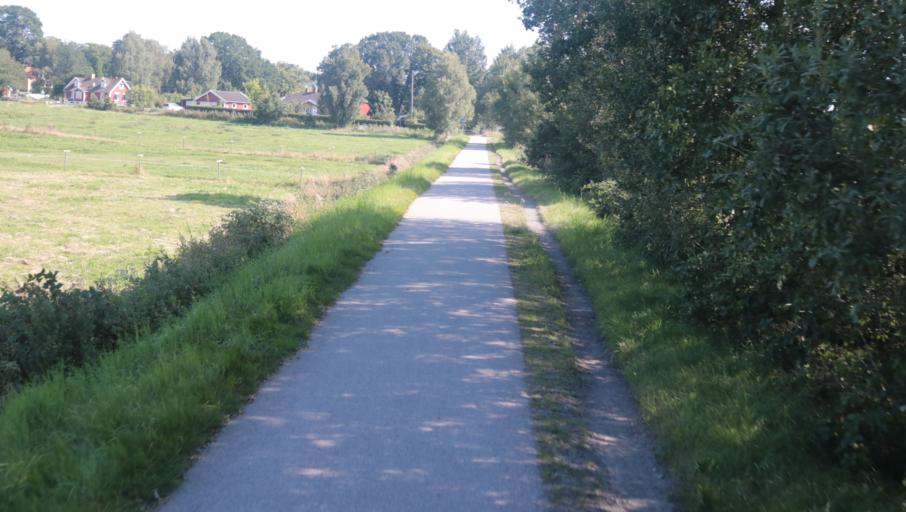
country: SE
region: Blekinge
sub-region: Karlshamns Kommun
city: Svangsta
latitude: 56.2348
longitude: 14.8071
